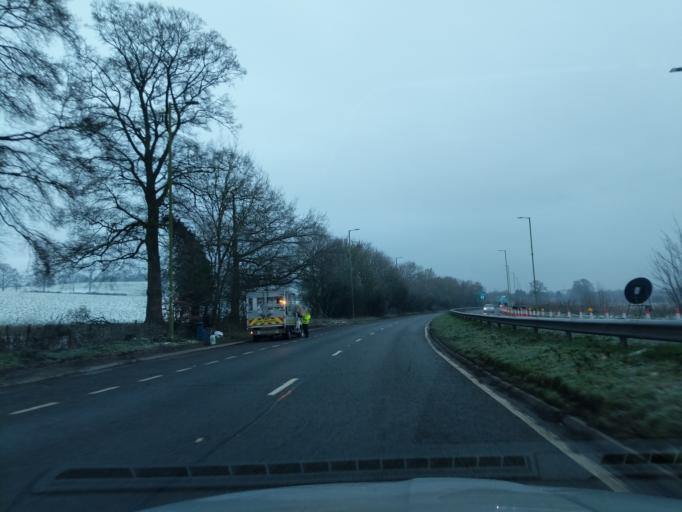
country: GB
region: England
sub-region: Hertfordshire
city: Kings Langley
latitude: 51.6949
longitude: -0.4389
